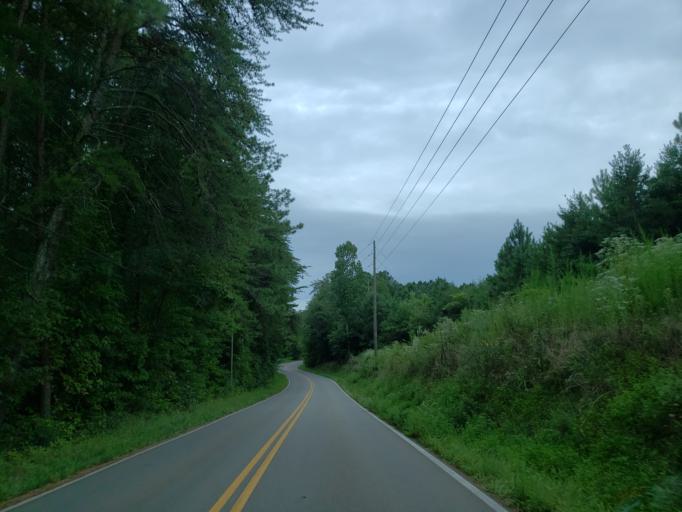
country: US
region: Georgia
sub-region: Pickens County
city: Jasper
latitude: 34.4203
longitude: -84.5760
